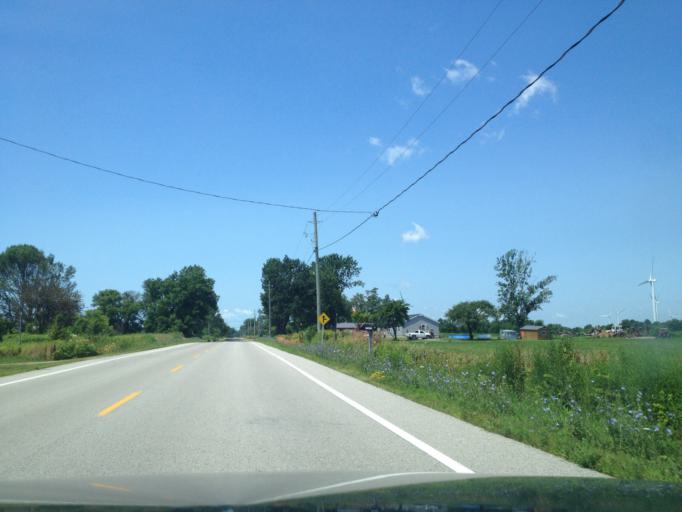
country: CA
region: Ontario
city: Norfolk County
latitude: 42.5804
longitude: -80.5777
